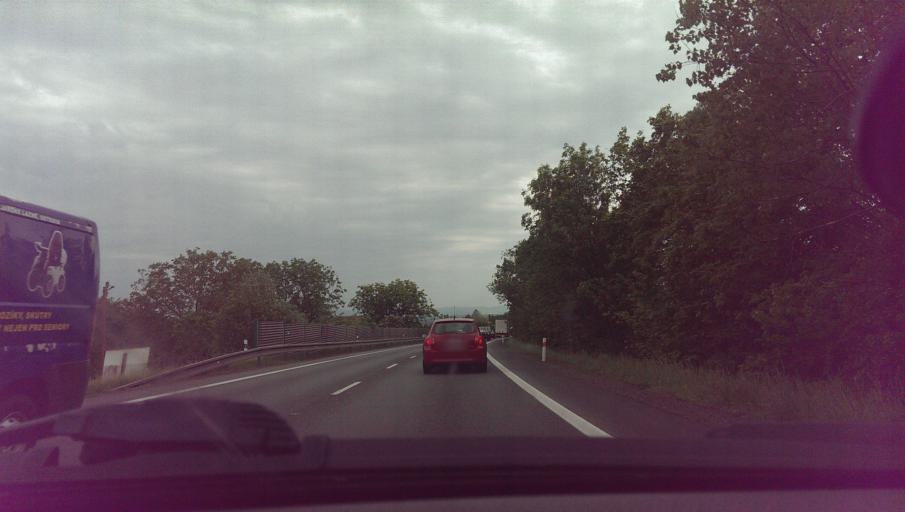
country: CZ
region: Zlin
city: Buchlovice
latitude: 49.0888
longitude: 17.3284
